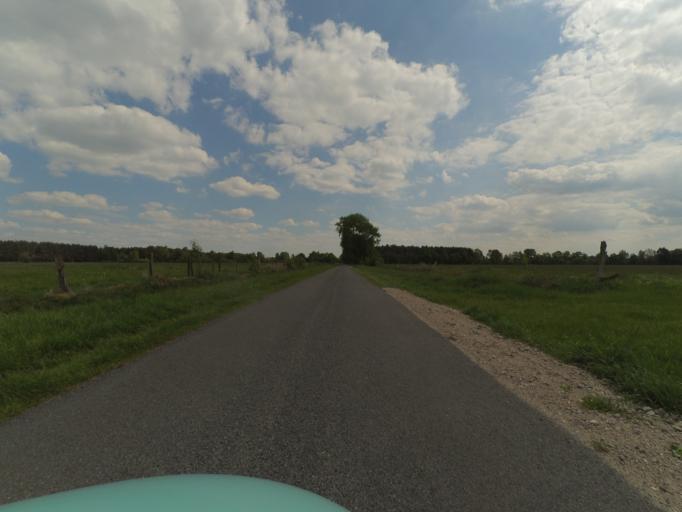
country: DE
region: Lower Saxony
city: Adelheidsdorf
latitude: 52.5704
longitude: 10.0185
